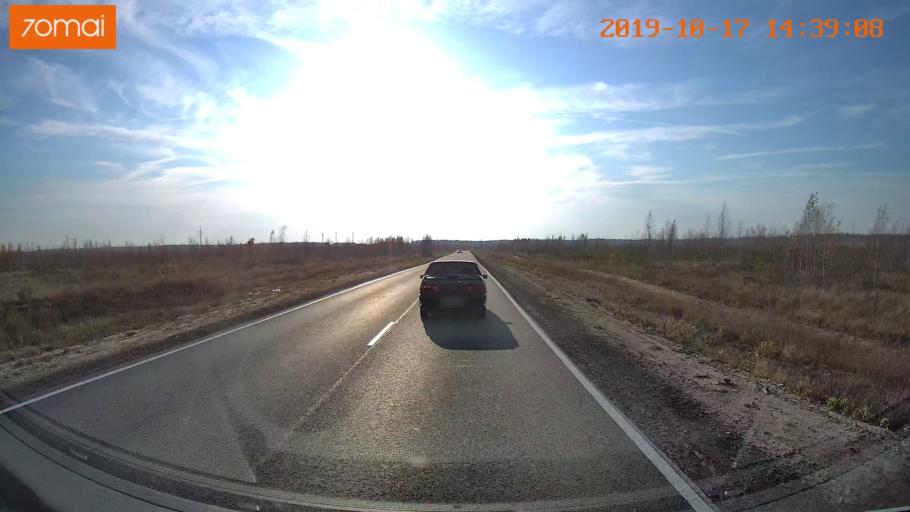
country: RU
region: Rjazan
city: Solotcha
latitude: 54.8644
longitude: 39.9765
